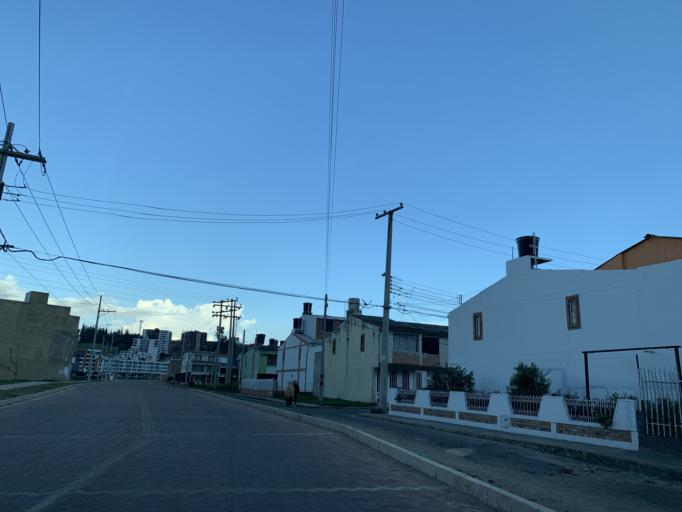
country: CO
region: Boyaca
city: Tunja
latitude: 5.5513
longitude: -73.3493
